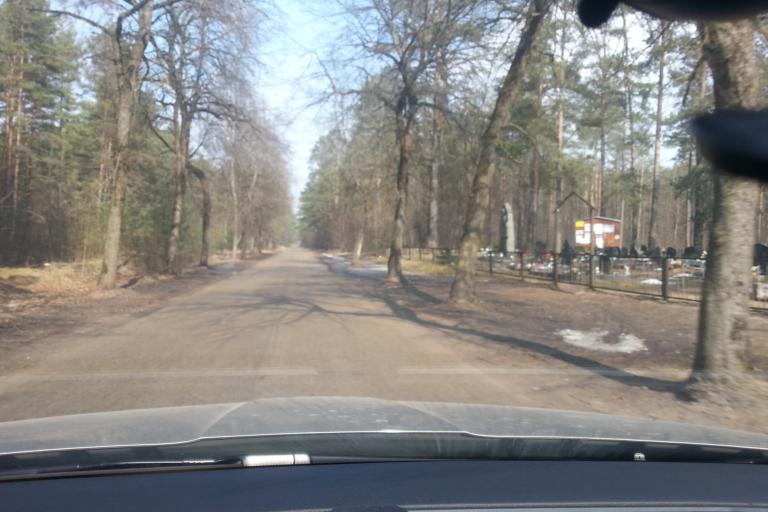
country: LT
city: Trakai
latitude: 54.5055
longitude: 24.9845
